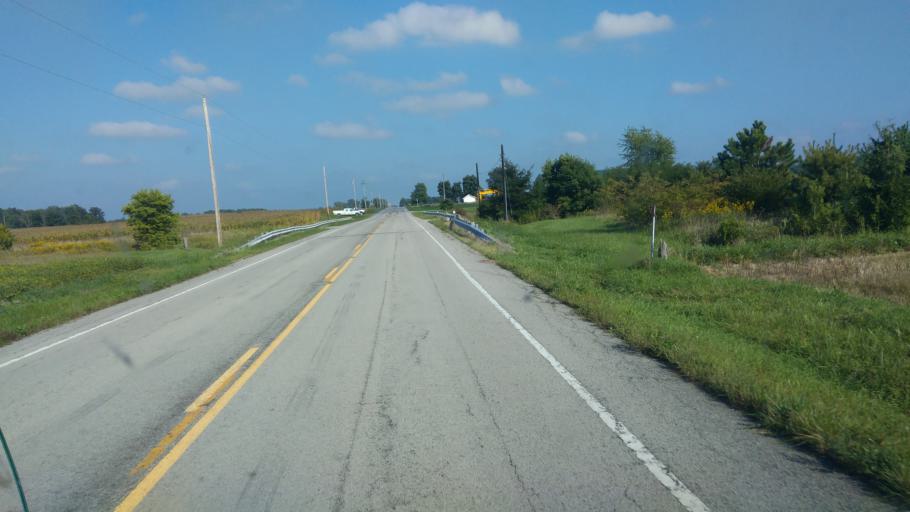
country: US
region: Ohio
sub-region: Hancock County
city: Arlington
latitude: 40.8337
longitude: -83.6032
